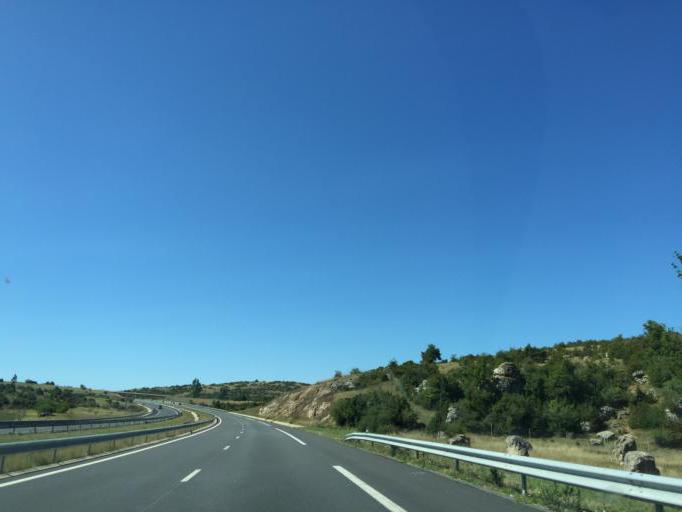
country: FR
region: Midi-Pyrenees
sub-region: Departement de l'Aveyron
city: La Cavalerie
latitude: 43.9045
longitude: 3.2748
